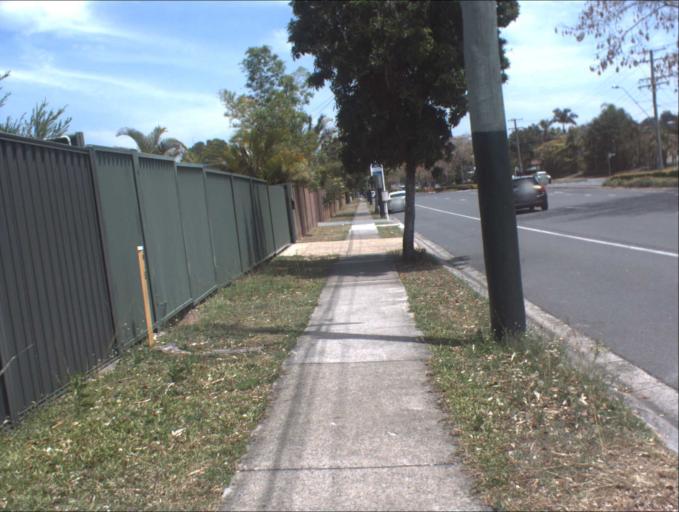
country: AU
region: Queensland
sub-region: Logan
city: Slacks Creek
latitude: -27.6348
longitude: 153.1450
